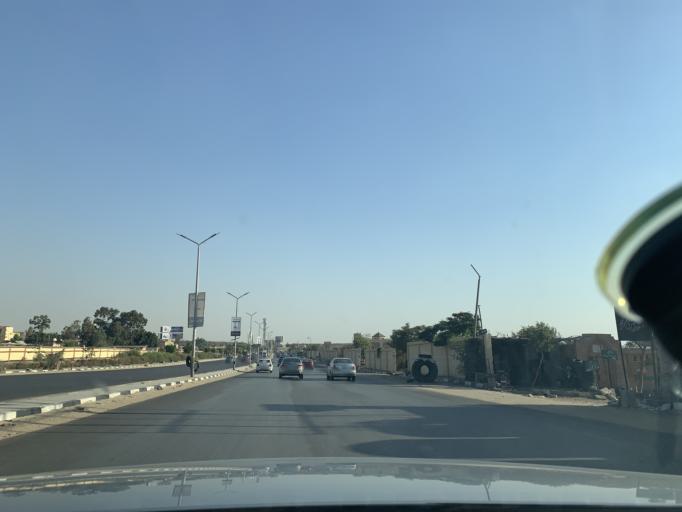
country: EG
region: Muhafazat al Qahirah
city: Cairo
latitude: 30.0299
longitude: 31.3542
